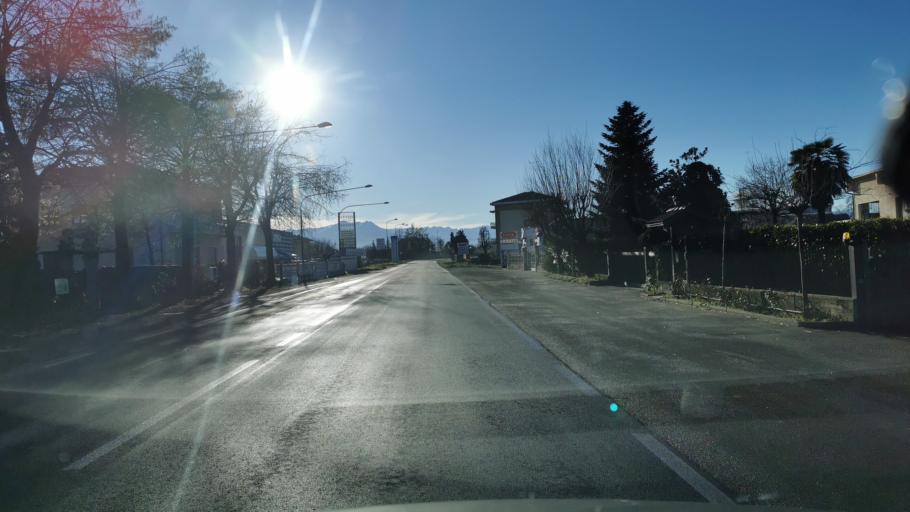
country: IT
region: Piedmont
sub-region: Provincia di Cuneo
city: Carru
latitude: 44.4762
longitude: 7.8636
